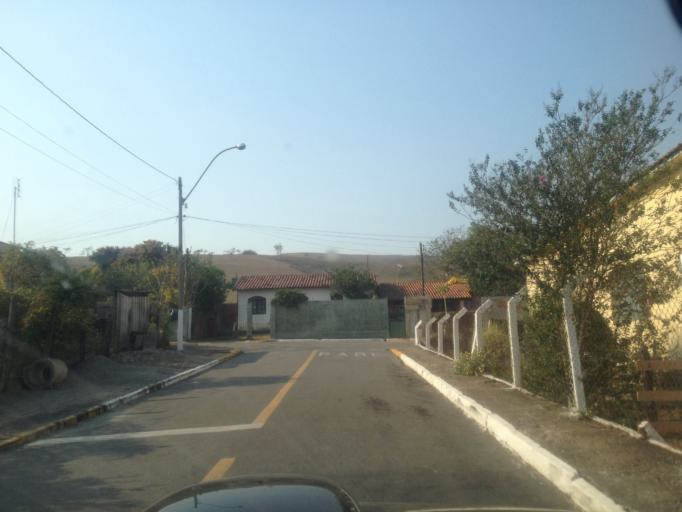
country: BR
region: Rio de Janeiro
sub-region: Porto Real
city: Porto Real
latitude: -22.4621
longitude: -44.3454
